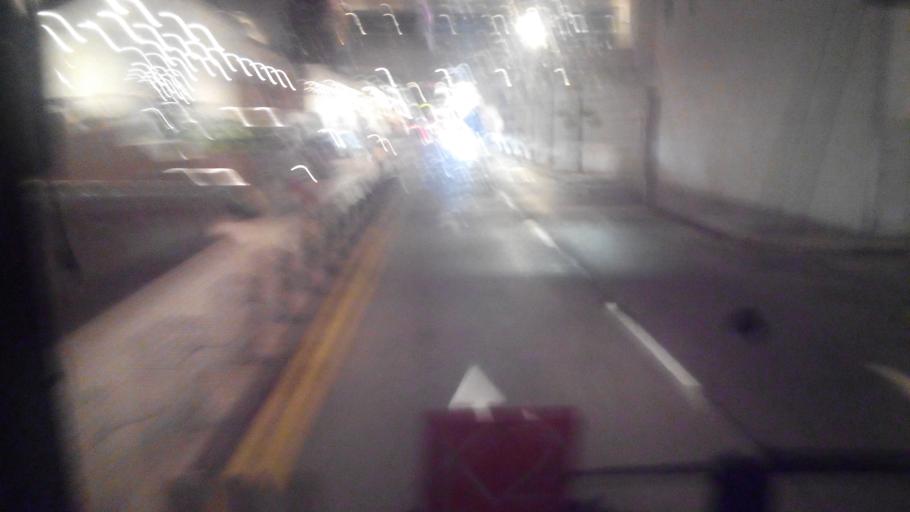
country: HK
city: Hong Kong
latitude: 22.2989
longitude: 114.1685
